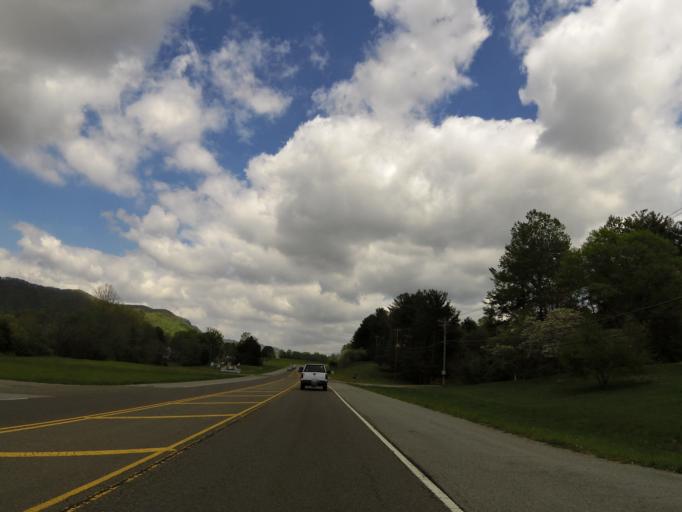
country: US
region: Tennessee
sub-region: Campbell County
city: LaFollette
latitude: 36.3938
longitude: -84.0921
